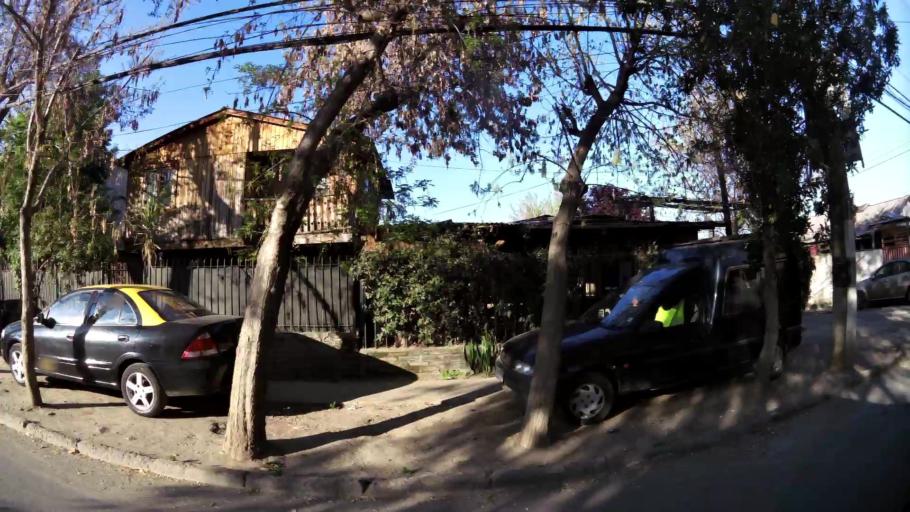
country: CL
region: Santiago Metropolitan
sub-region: Provincia de Santiago
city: Santiago
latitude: -33.3779
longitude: -70.6181
